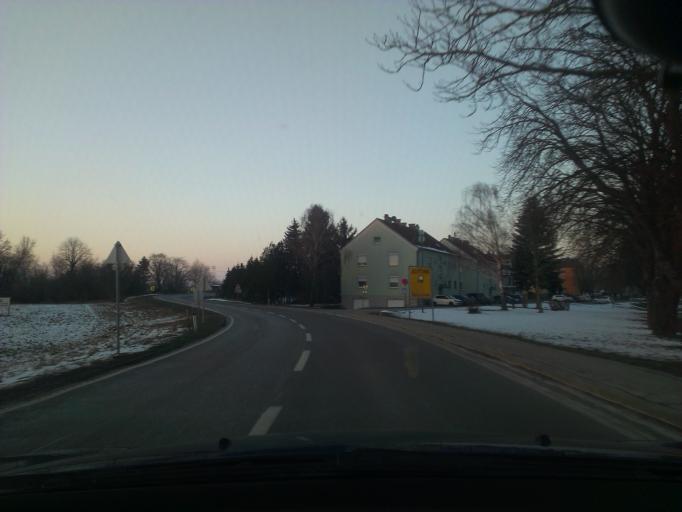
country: AT
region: Lower Austria
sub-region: Politischer Bezirk Bruck an der Leitha
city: Gotzendorf an der Leitha
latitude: 48.0166
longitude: 16.5826
